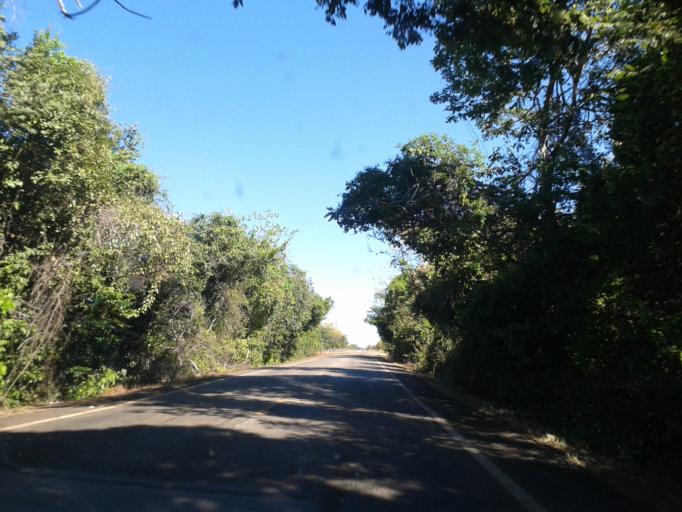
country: BR
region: Goias
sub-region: Crixas
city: Crixas
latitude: -14.0260
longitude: -50.3274
